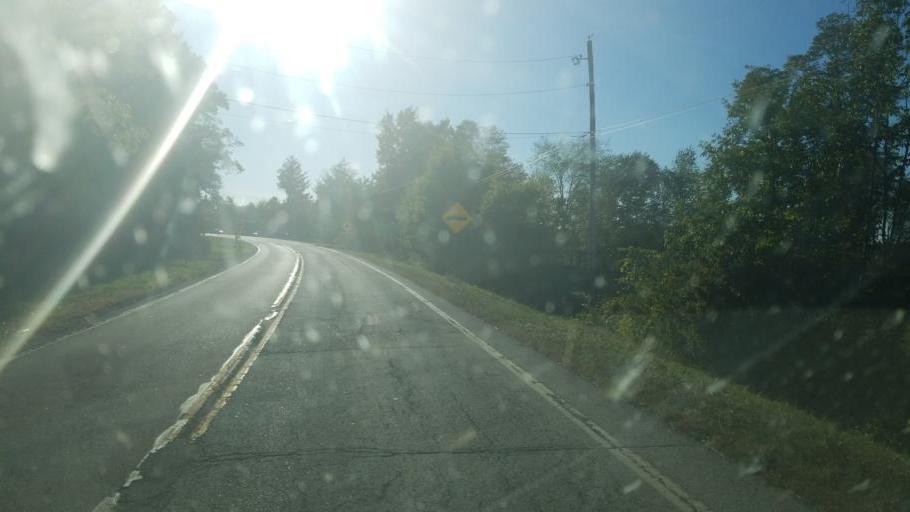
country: US
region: Ohio
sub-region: Richland County
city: Lexington
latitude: 40.6241
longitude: -82.6604
